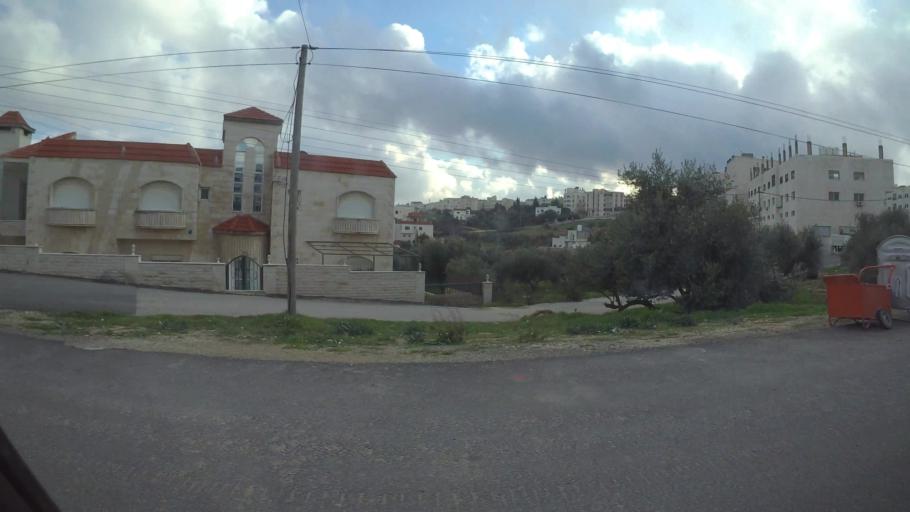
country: JO
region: Amman
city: Al Jubayhah
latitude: 32.0548
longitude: 35.8907
